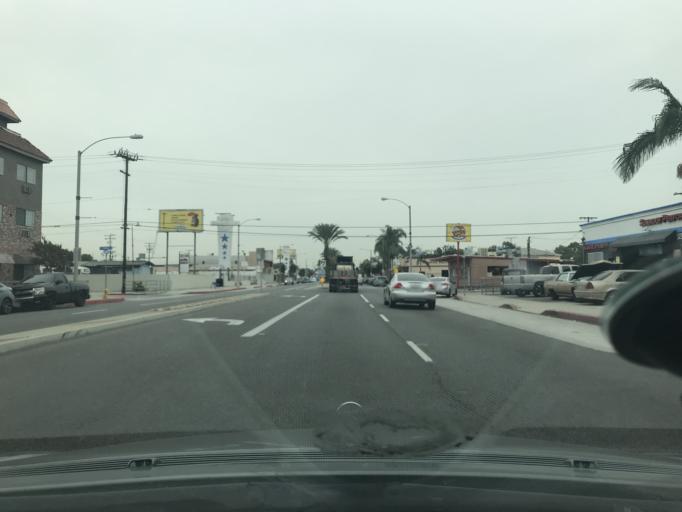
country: US
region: California
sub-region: Los Angeles County
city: Cudahy
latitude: 33.9368
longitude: -118.1821
